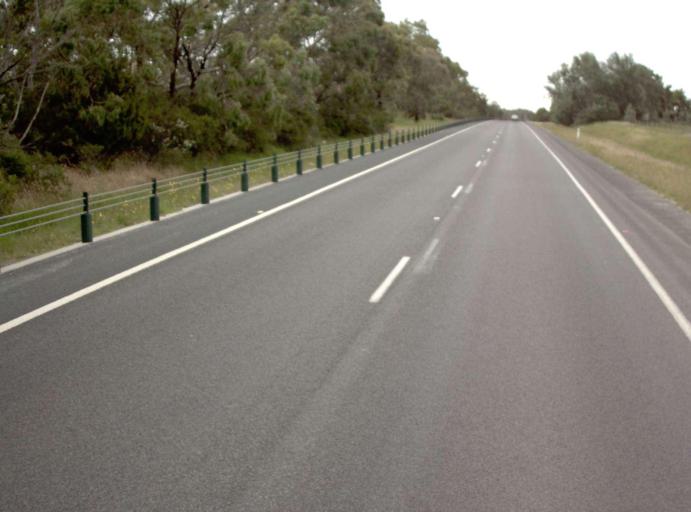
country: AU
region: Victoria
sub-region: Casey
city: Junction Village
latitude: -38.1434
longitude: 145.3109
